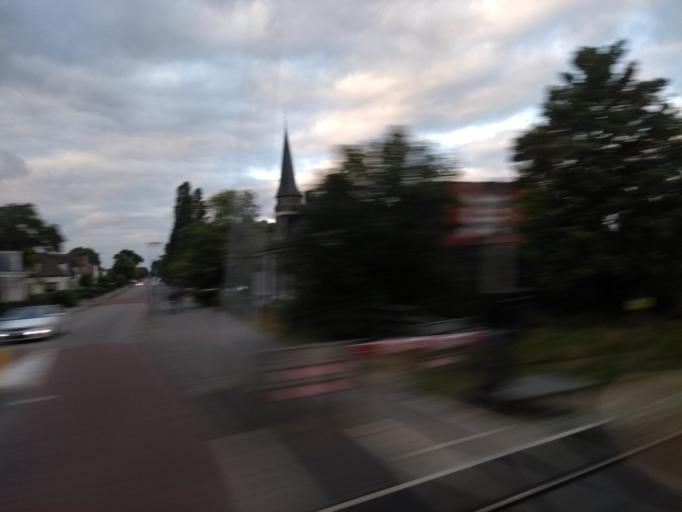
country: NL
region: Friesland
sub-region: Gemeente Weststellingwerf
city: Wolvega
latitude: 52.8779
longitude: 6.0074
